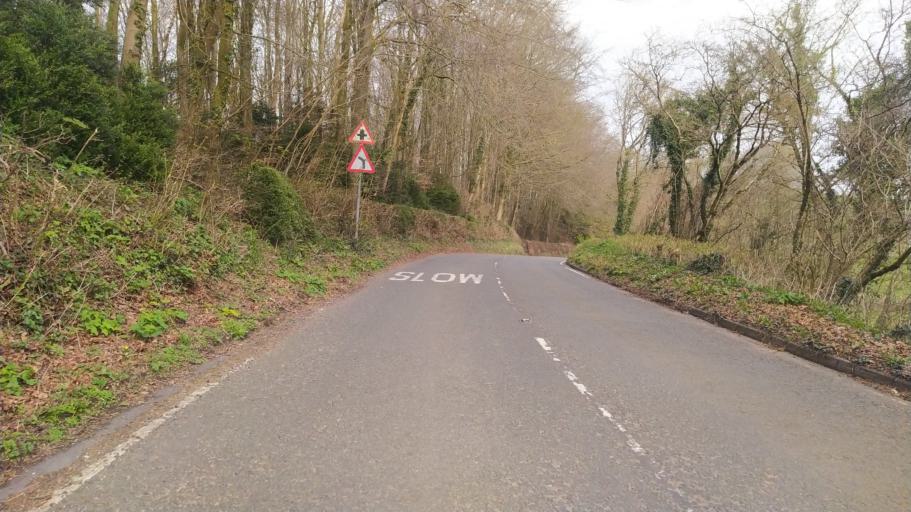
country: GB
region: England
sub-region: Dorset
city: Beaminster
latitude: 50.8504
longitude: -2.7230
